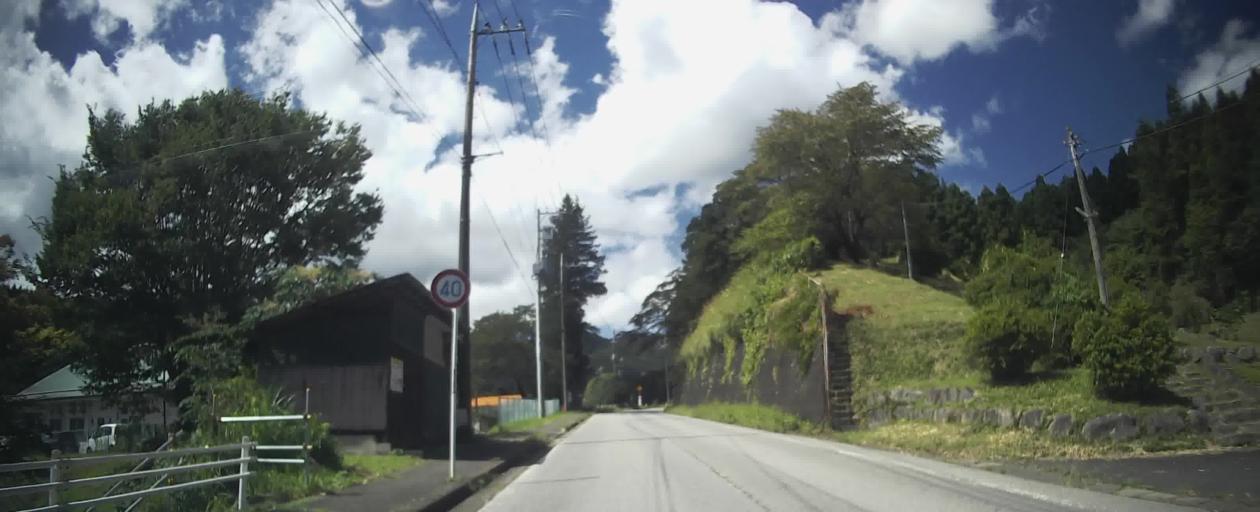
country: JP
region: Gunma
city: Kanekomachi
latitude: 36.4370
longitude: 138.9169
